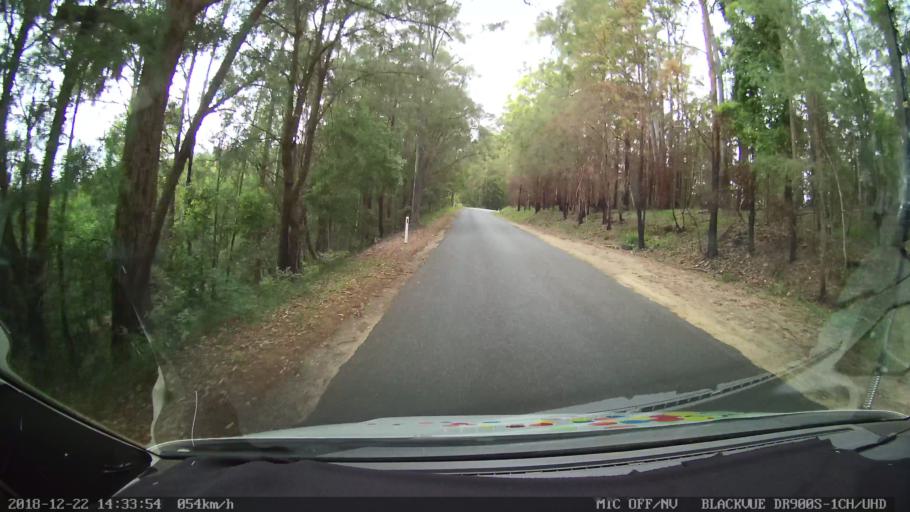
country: AU
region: New South Wales
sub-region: Bellingen
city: Dorrigo
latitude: -30.1161
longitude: 152.6221
